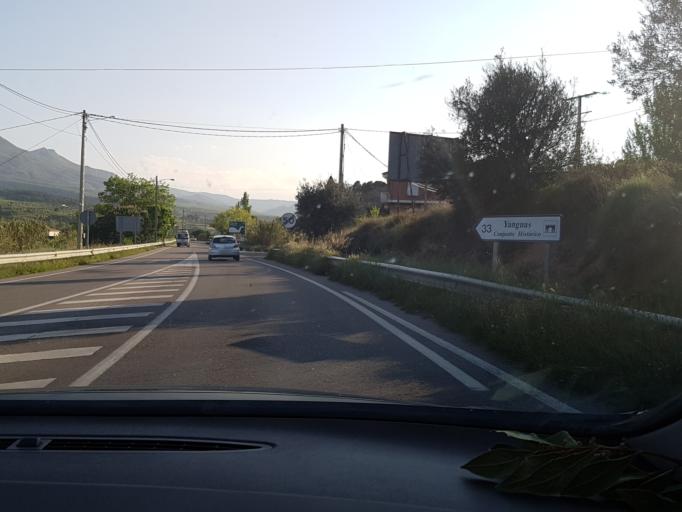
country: ES
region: La Rioja
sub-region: Provincia de La Rioja
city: Arnedo
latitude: 42.2196
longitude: -2.1184
